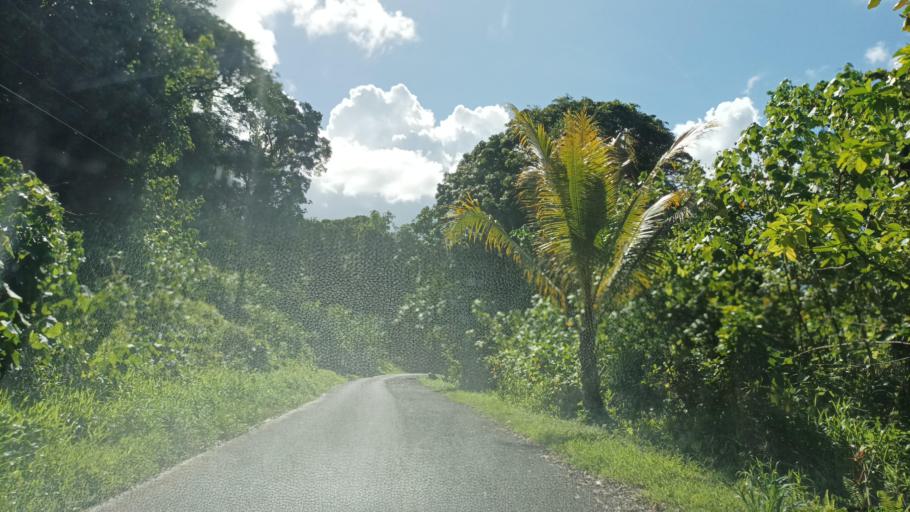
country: FM
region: Pohnpei
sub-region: Madolenihm Municipality
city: Madolenihm Municipality Government
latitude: 6.8554
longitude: 158.2954
